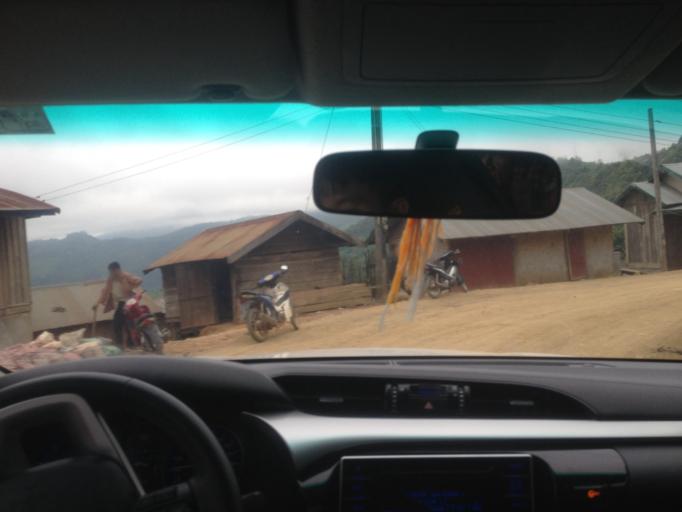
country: TH
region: Nan
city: Chaloem Phra Kiat
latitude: 19.9842
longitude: 101.1433
